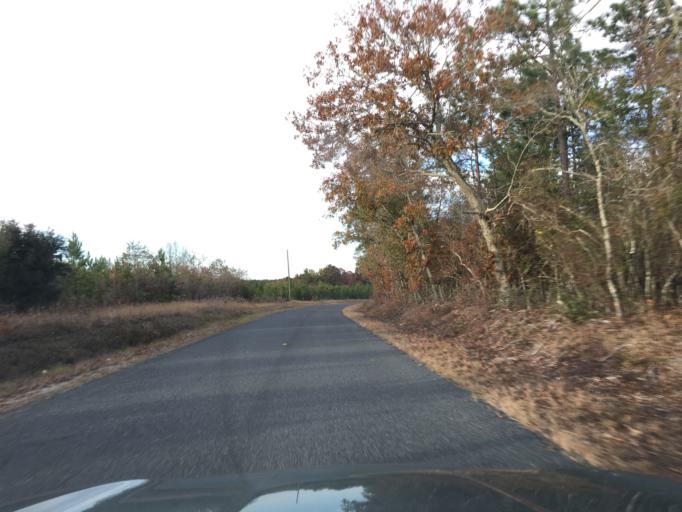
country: US
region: South Carolina
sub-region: Barnwell County
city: Williston
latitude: 33.6678
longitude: -81.3717
